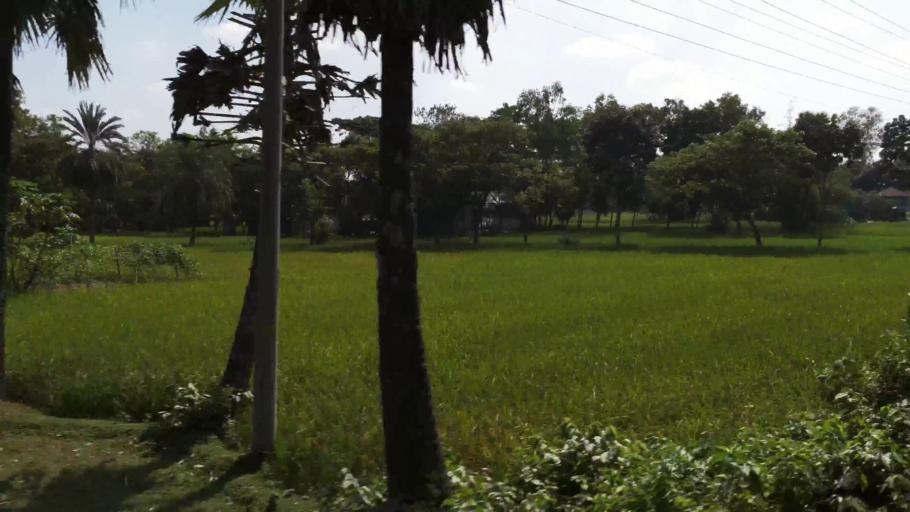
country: BD
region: Dhaka
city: Gafargaon
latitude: 24.2253
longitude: 90.4875
